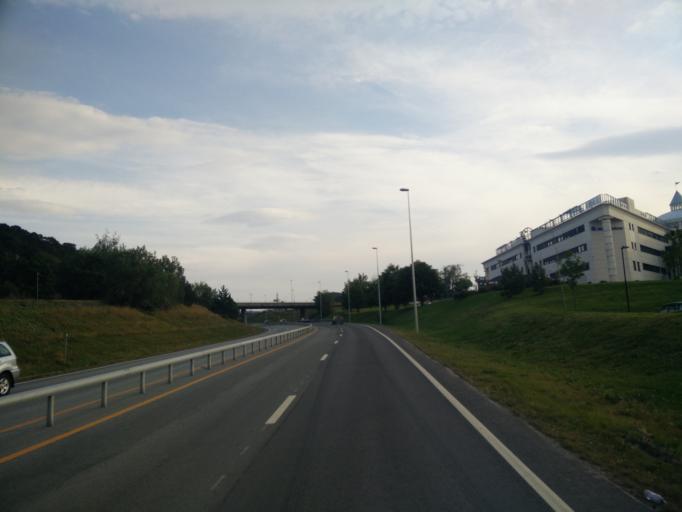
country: NO
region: Sor-Trondelag
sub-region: Trondheim
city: Trondheim
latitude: 63.4351
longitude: 10.4727
